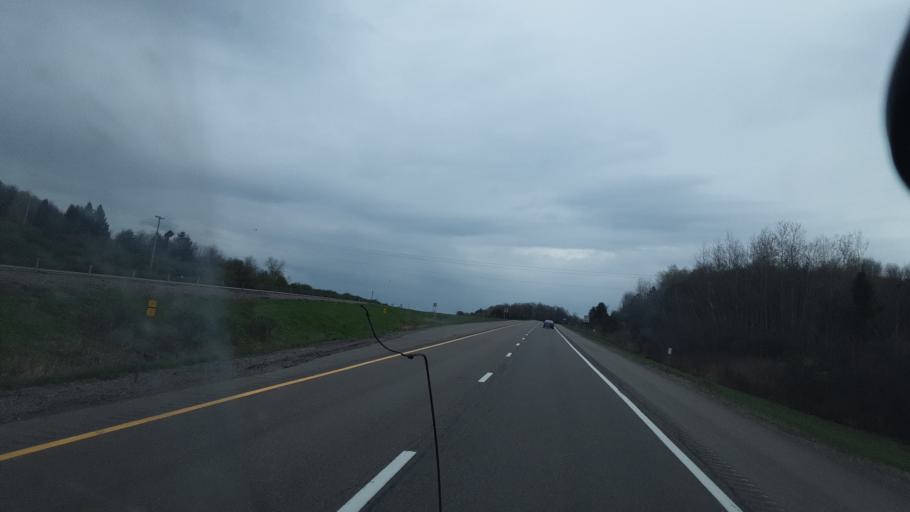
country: US
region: New York
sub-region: Allegany County
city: Alfred
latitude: 42.3076
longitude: -77.8682
